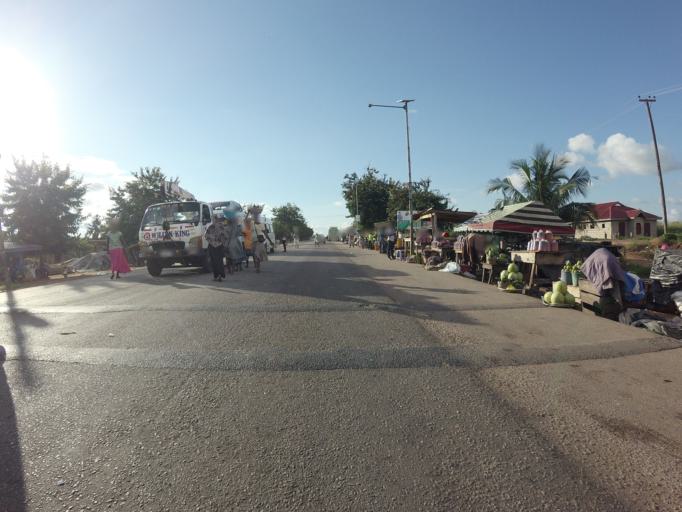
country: GH
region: Ashanti
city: Tafo
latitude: 6.9194
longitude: -1.6604
